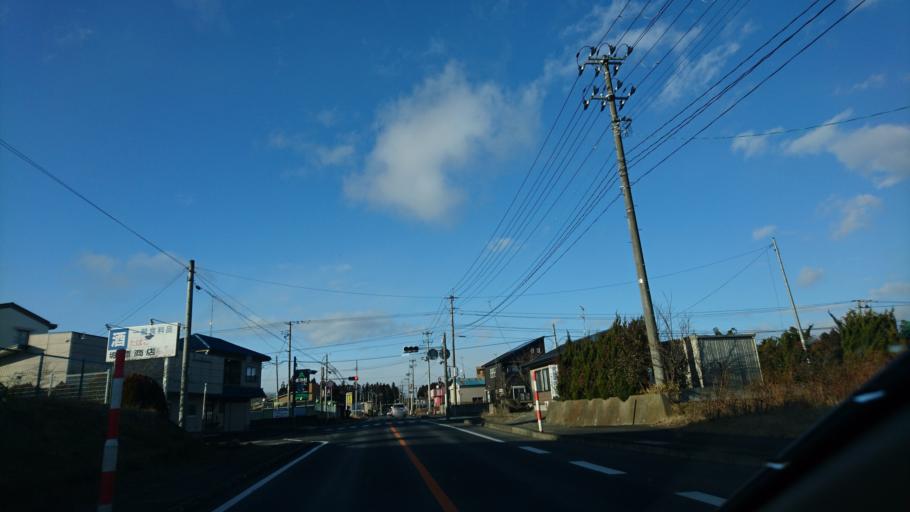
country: JP
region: Miyagi
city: Tomiya
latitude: 38.4643
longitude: 140.8705
